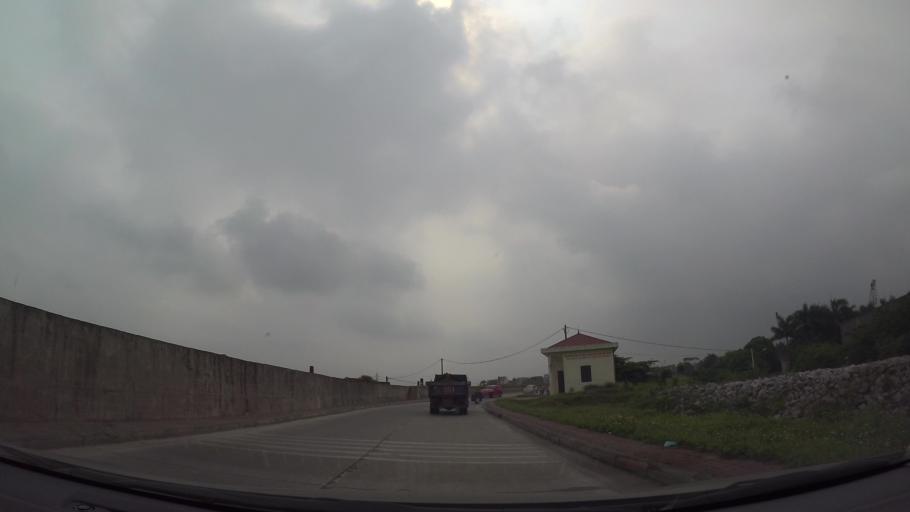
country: VN
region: Ha Noi
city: Trau Quy
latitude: 21.0758
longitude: 105.9132
